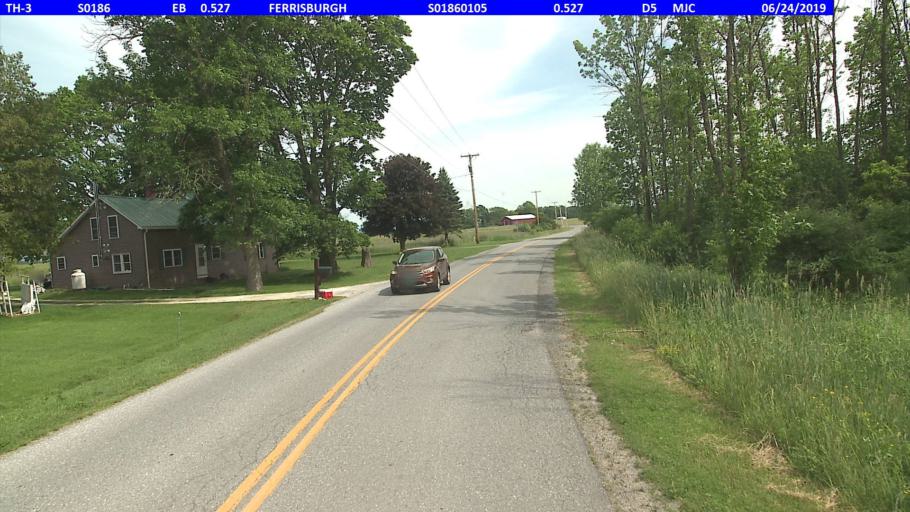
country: US
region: Vermont
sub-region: Addison County
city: Vergennes
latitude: 44.1943
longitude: -73.3531
